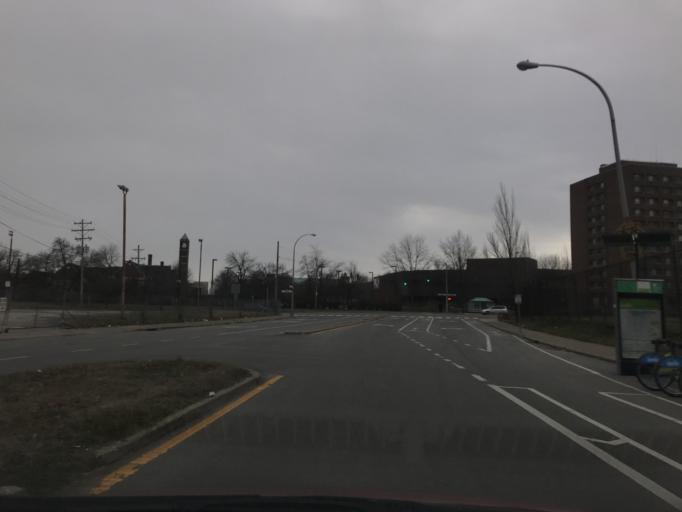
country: US
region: Kentucky
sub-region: Jefferson County
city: Louisville
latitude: 38.2209
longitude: -85.7563
